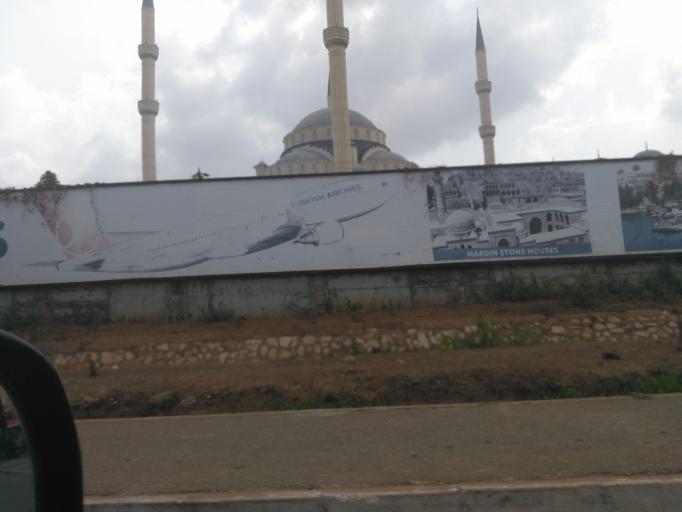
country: GH
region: Greater Accra
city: Accra
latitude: 5.5912
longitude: -0.1903
